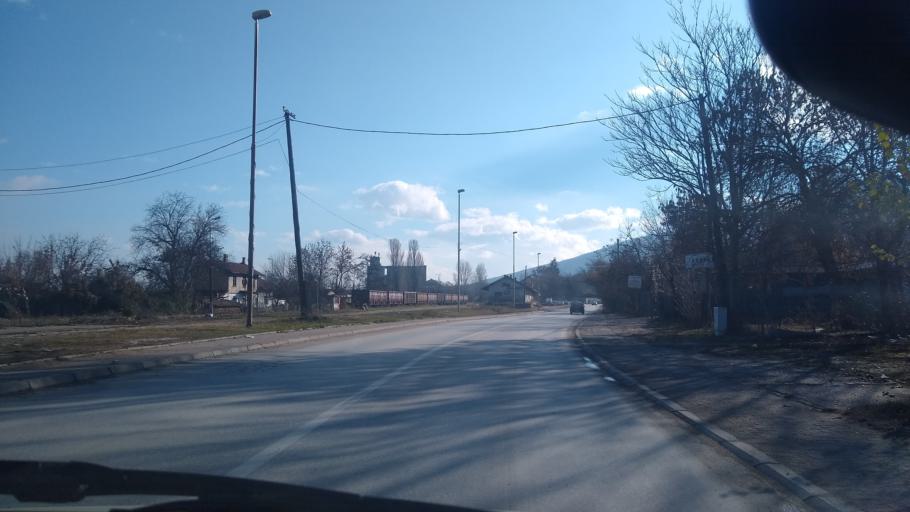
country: MK
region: Bitola
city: Bitola
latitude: 41.0222
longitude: 21.3422
